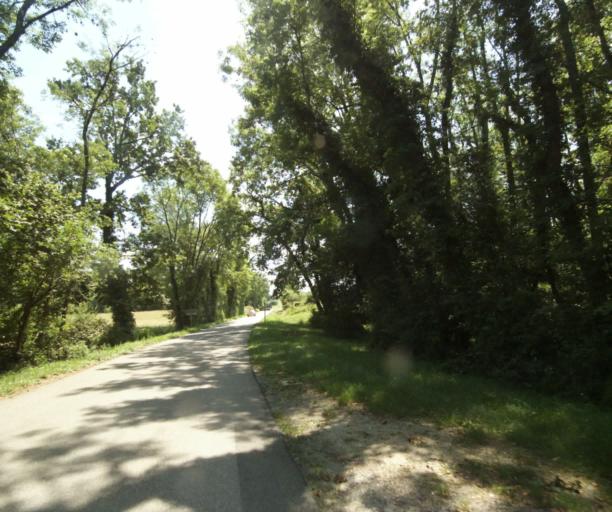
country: FR
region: Rhone-Alpes
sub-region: Departement de la Haute-Savoie
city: Messery
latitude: 46.3630
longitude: 6.3102
